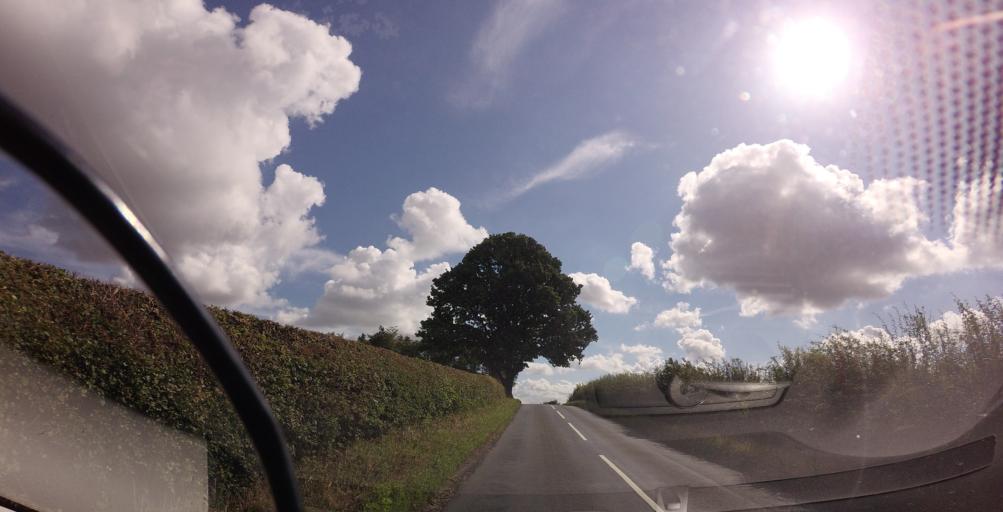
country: GB
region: England
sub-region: North Yorkshire
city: Boroughbridge
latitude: 54.0484
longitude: -1.3918
